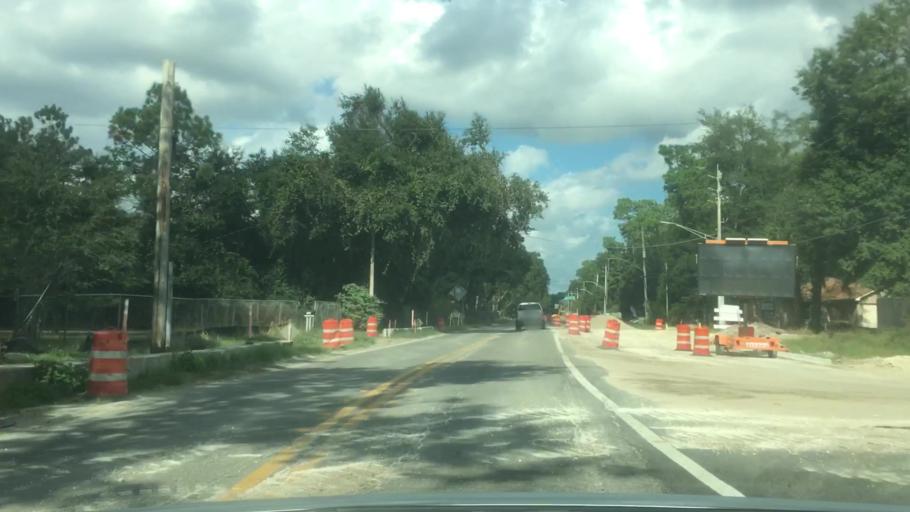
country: US
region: Florida
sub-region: Duval County
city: Atlantic Beach
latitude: 30.3454
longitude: -81.4613
